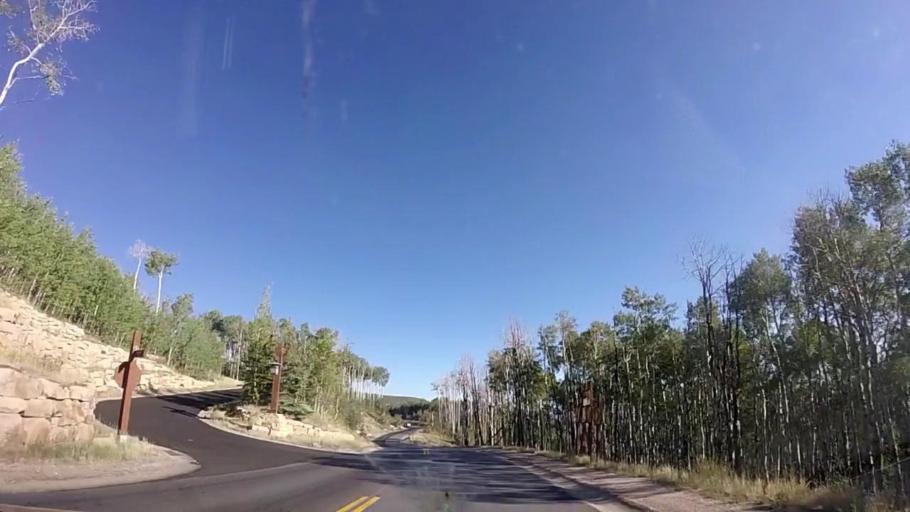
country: US
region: Utah
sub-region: Summit County
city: Park City
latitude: 40.6233
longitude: -111.4987
